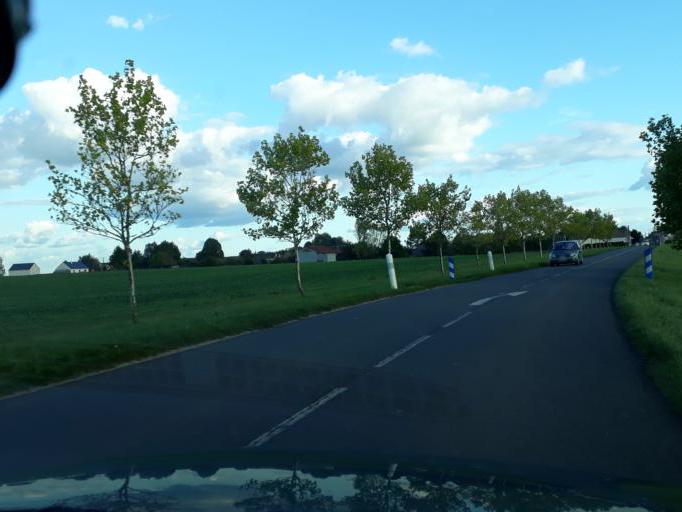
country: FR
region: Centre
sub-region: Departement du Loir-et-Cher
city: Mer
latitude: 47.8006
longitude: 1.5194
